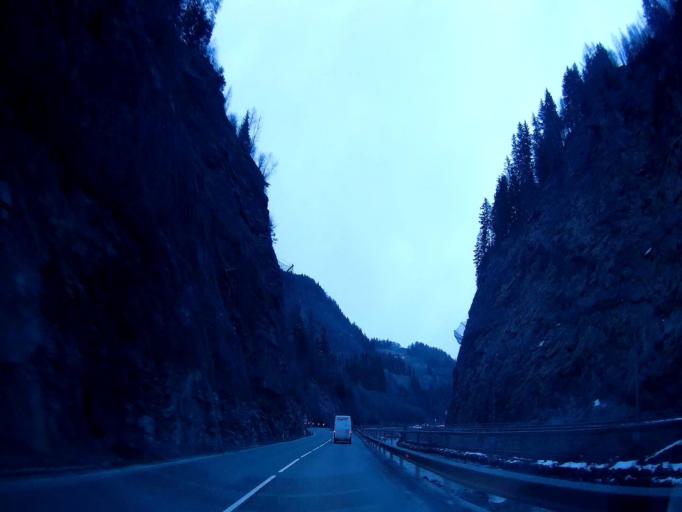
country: AT
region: Salzburg
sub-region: Politischer Bezirk Sankt Johann im Pongau
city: Goldegg
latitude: 47.3050
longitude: 13.1103
